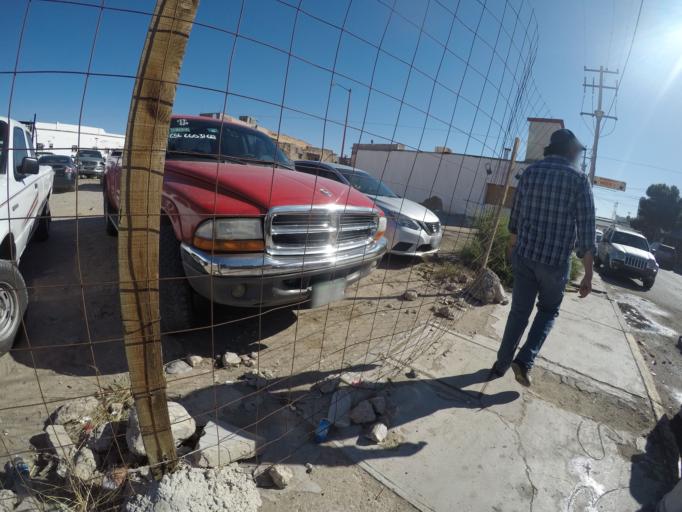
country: MX
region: Chihuahua
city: Ciudad Juarez
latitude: 31.7419
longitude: -106.4859
